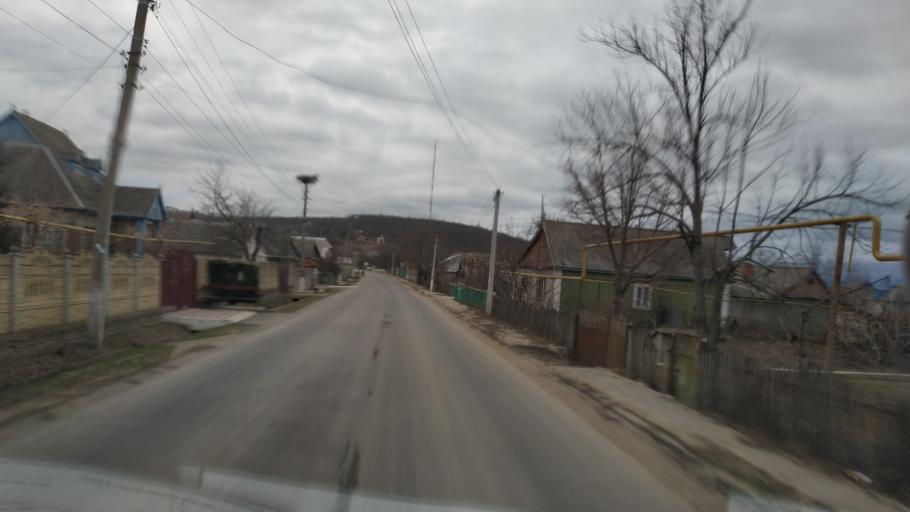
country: MD
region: Causeni
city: Causeni
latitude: 46.6509
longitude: 29.4419
